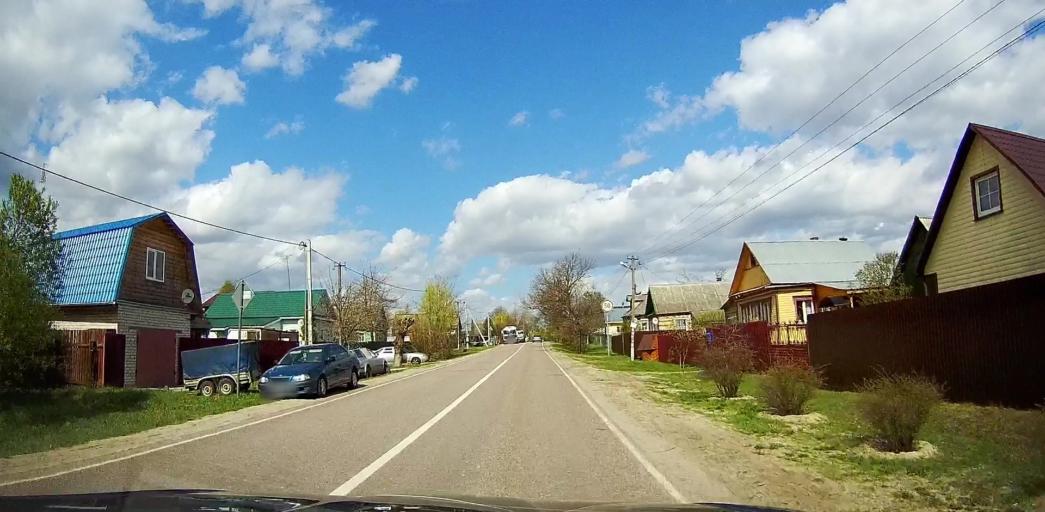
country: RU
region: Moskovskaya
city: Davydovo
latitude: 55.5742
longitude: 38.8199
